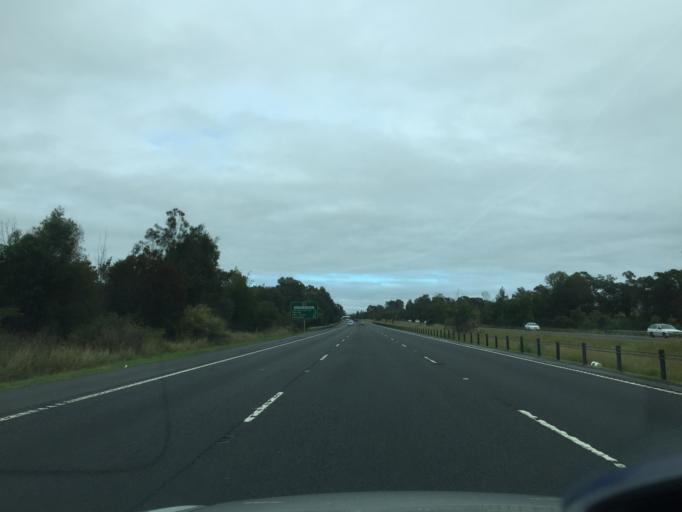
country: AU
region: New South Wales
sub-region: Penrith Municipality
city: Werrington County
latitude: -33.7832
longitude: 150.7588
